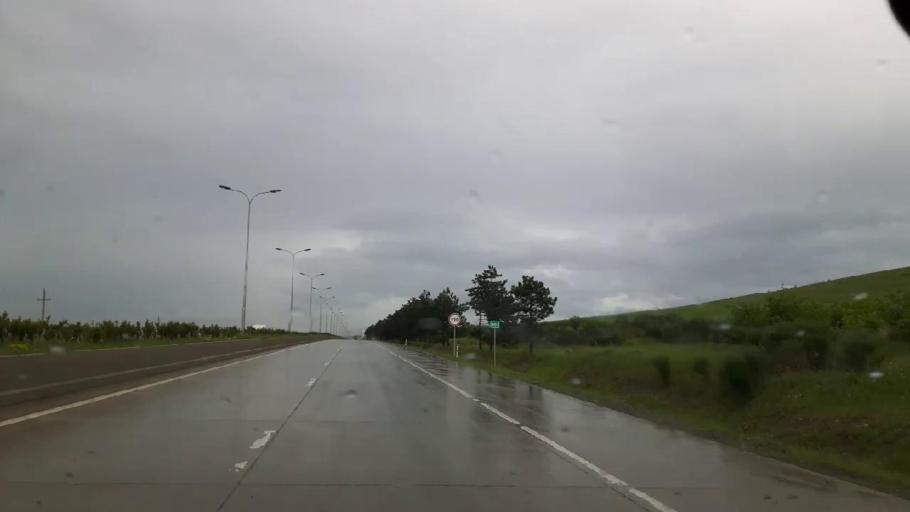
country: GE
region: Shida Kartli
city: Gori
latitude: 42.0181
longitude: 44.0200
